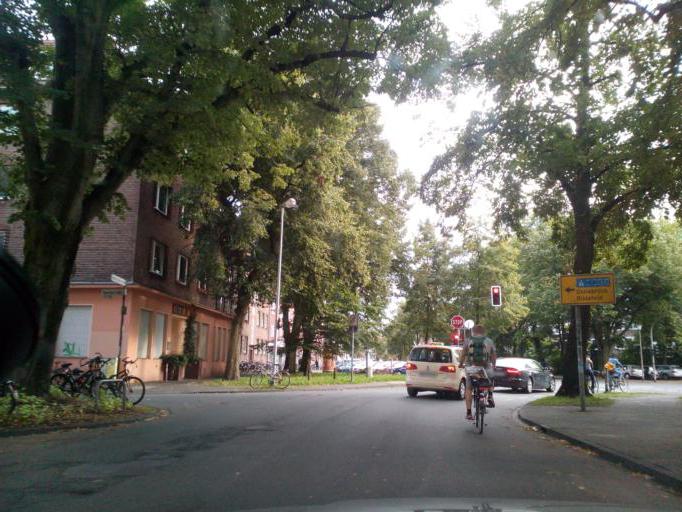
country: DE
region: North Rhine-Westphalia
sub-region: Regierungsbezirk Munster
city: Muenster
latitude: 51.9512
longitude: 7.6319
